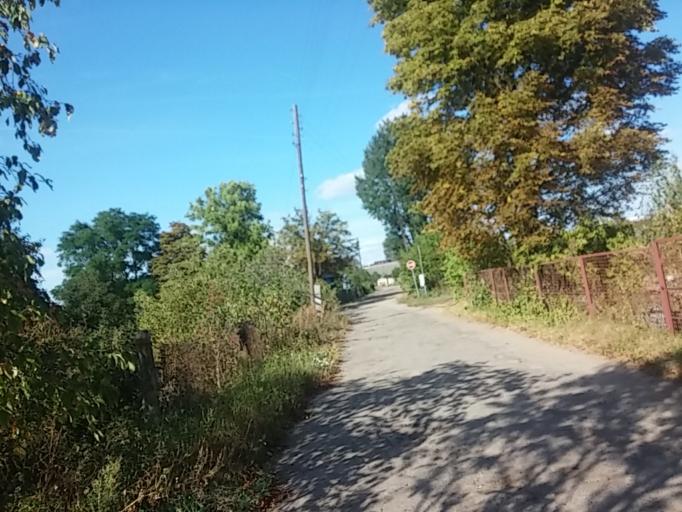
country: BY
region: Minsk
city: Chervyen'
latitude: 53.7765
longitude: 28.2665
